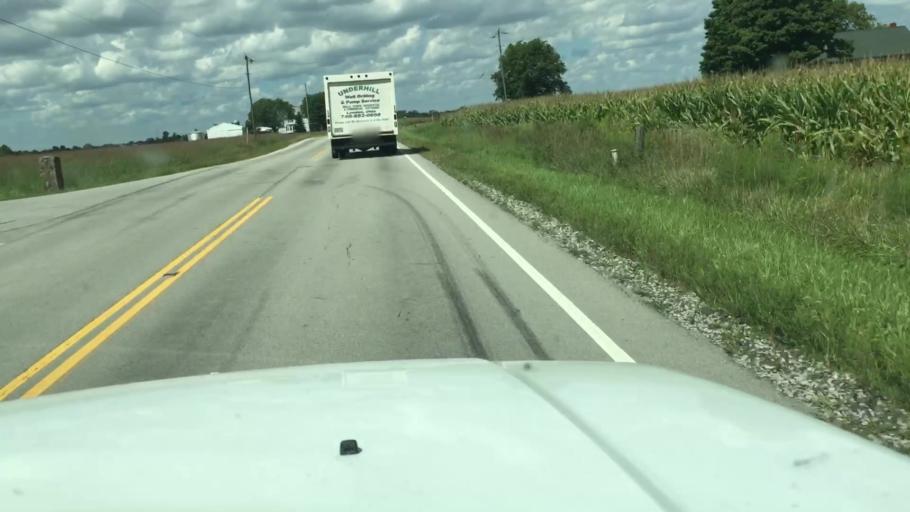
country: US
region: Ohio
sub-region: Madison County
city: Bethel
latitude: 39.8190
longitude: -83.3566
